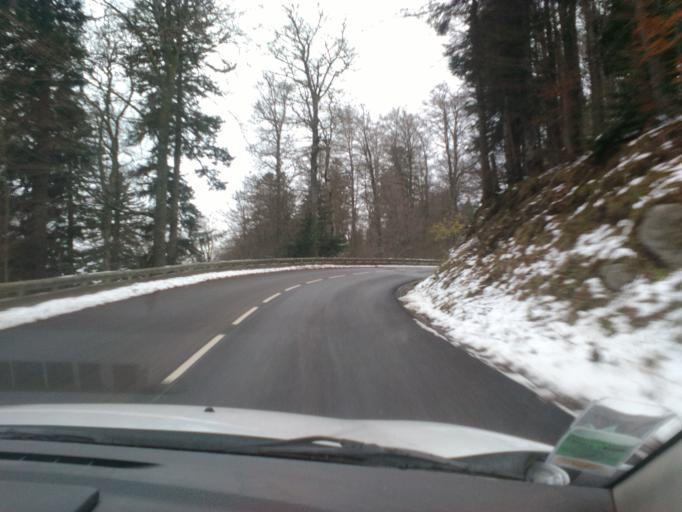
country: FR
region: Alsace
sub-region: Departement du Haut-Rhin
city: Metzeral
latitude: 48.0480
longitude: 7.0025
